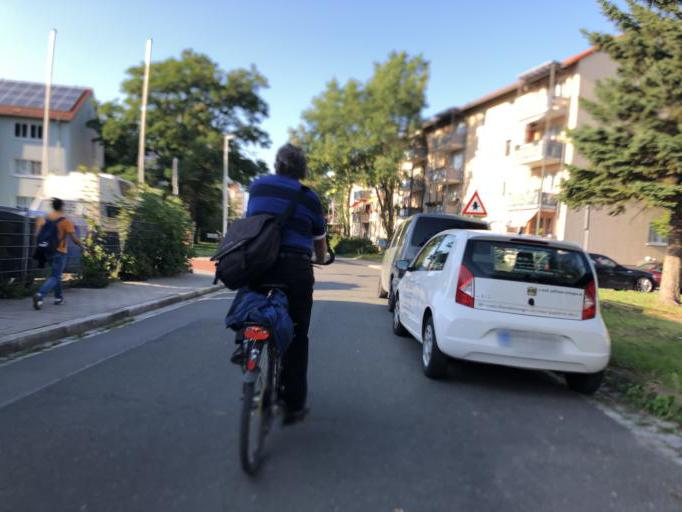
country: DE
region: Bavaria
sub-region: Regierungsbezirk Mittelfranken
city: Erlangen
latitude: 49.5840
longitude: 10.9992
